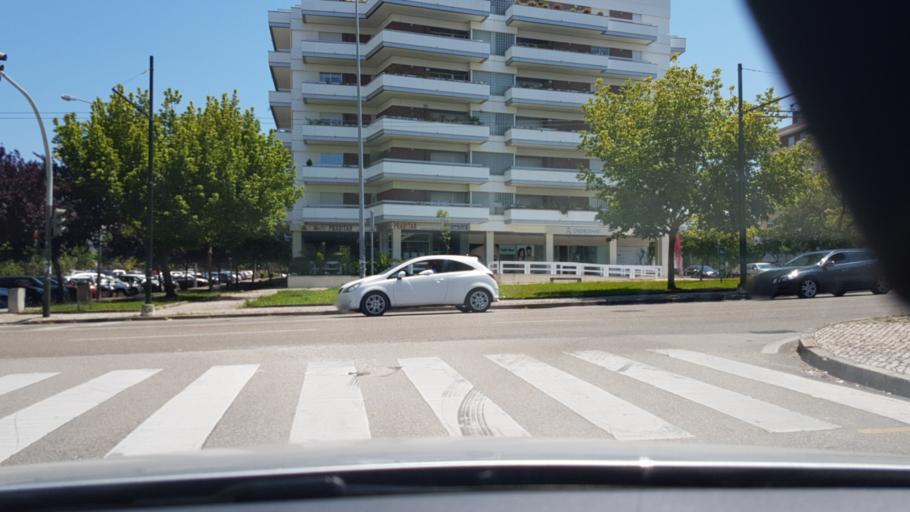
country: PT
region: Coimbra
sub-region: Coimbra
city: Coimbra
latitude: 40.2032
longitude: -8.4044
